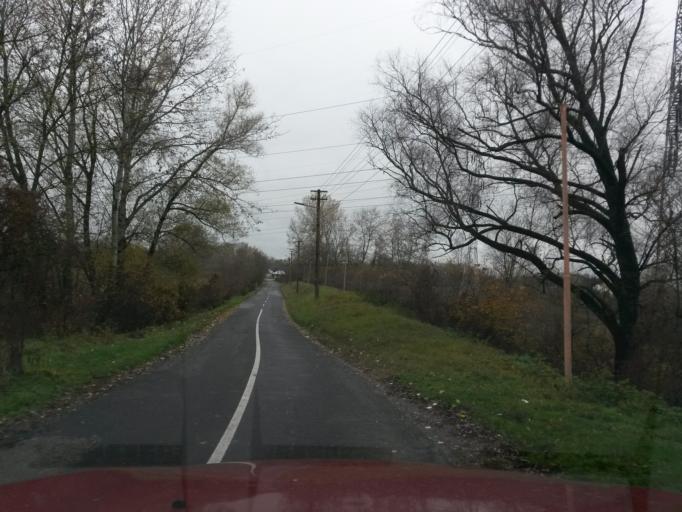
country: SK
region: Kosicky
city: Cierna nad Tisou
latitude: 48.5534
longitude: 21.9566
